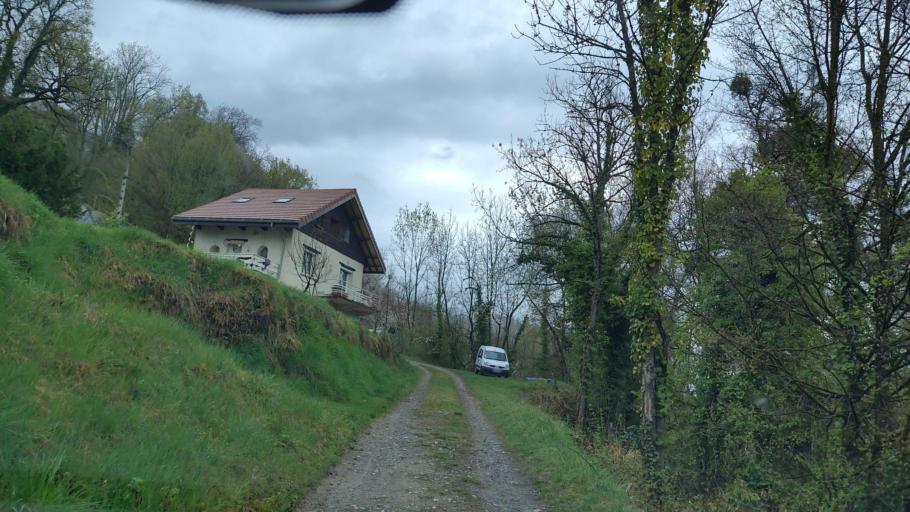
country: FR
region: Rhone-Alpes
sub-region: Departement de la Savoie
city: Frontenex
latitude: 45.6399
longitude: 6.3032
